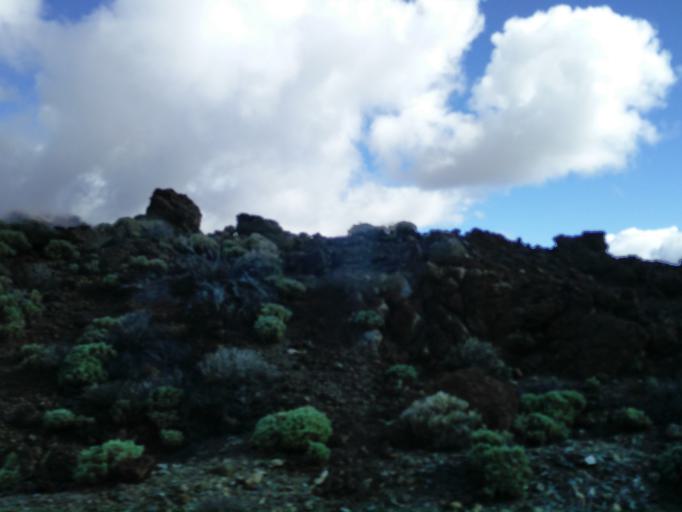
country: ES
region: Canary Islands
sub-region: Provincia de Santa Cruz de Tenerife
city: Vilaflor
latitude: 28.2113
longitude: -16.6580
